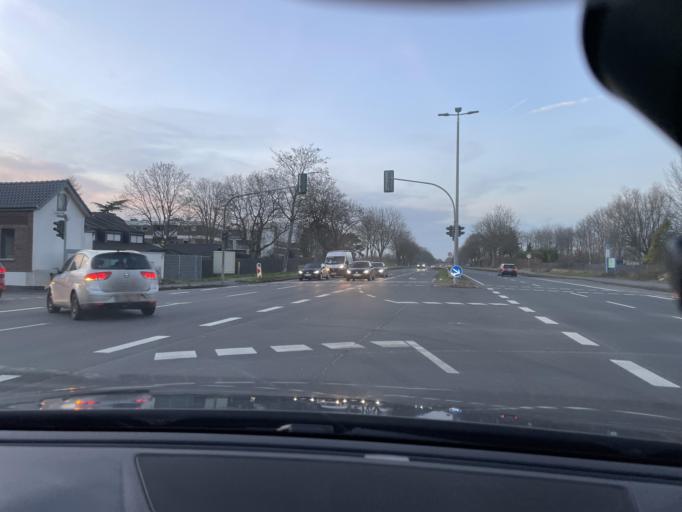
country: DE
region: North Rhine-Westphalia
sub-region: Regierungsbezirk Dusseldorf
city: Viersen
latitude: 51.2373
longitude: 6.4140
